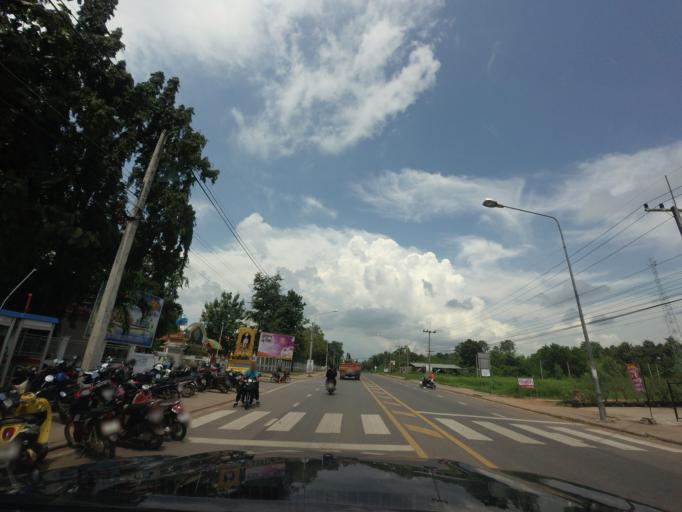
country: TH
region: Khon Kaen
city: Phu Wiang
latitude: 16.6593
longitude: 102.3691
